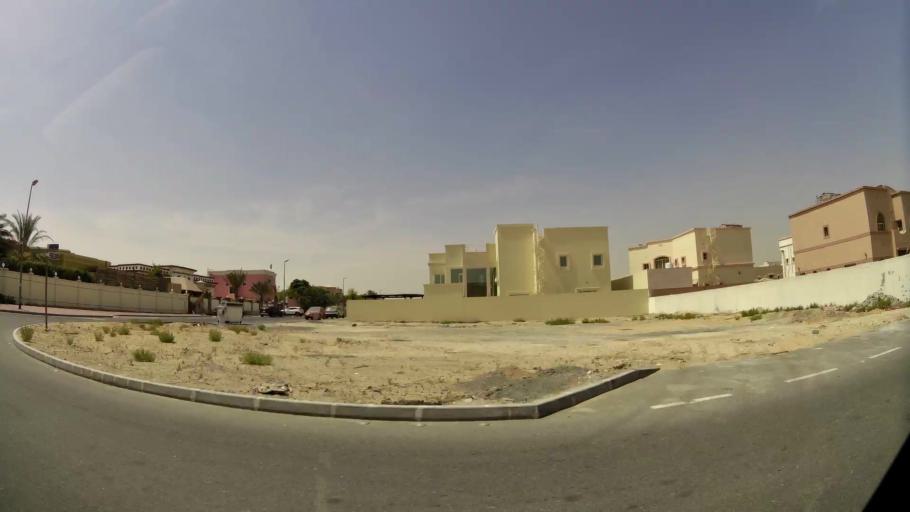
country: AE
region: Ash Shariqah
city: Sharjah
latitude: 25.1860
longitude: 55.4118
